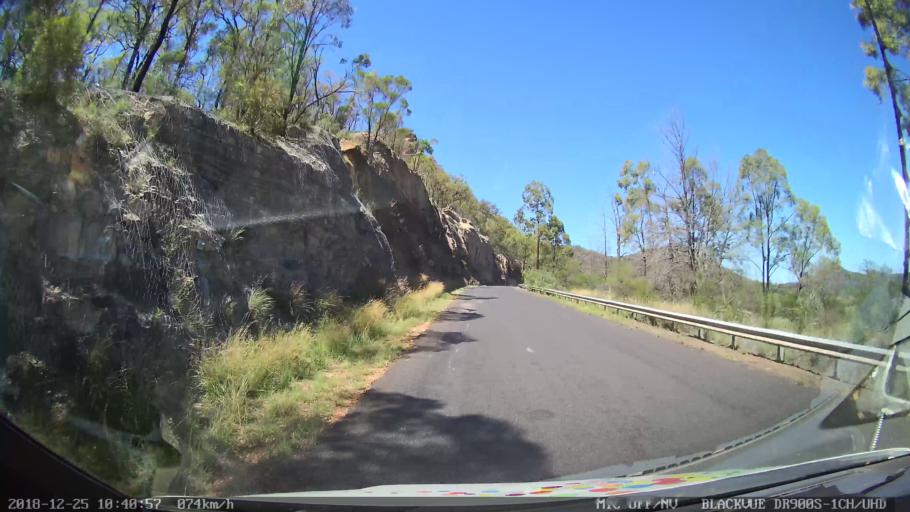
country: AU
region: New South Wales
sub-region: Upper Hunter Shire
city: Merriwa
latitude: -32.4129
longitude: 150.3395
